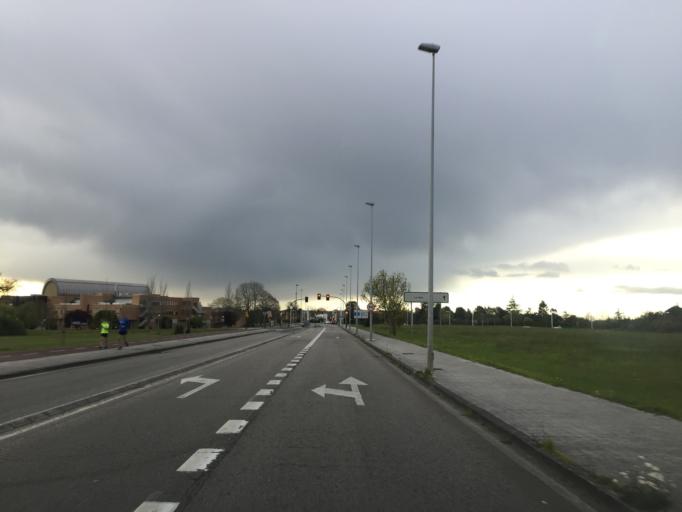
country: ES
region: Asturias
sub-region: Province of Asturias
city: Gijon
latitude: 43.5256
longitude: -5.6254
